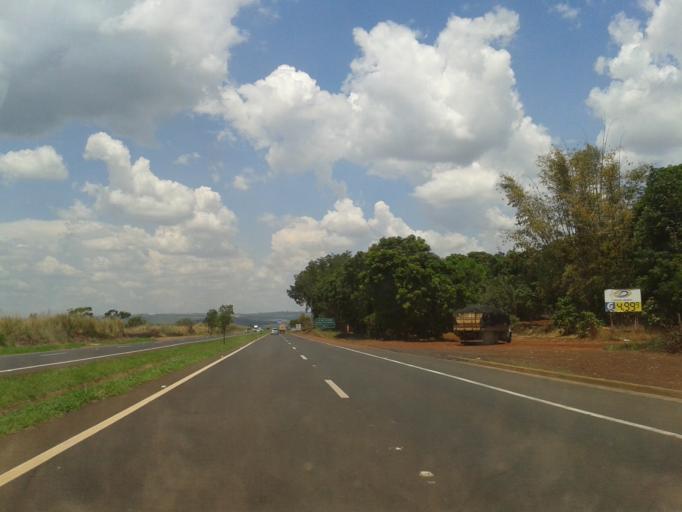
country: BR
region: Minas Gerais
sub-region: Araguari
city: Araguari
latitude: -18.7378
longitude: -48.2281
